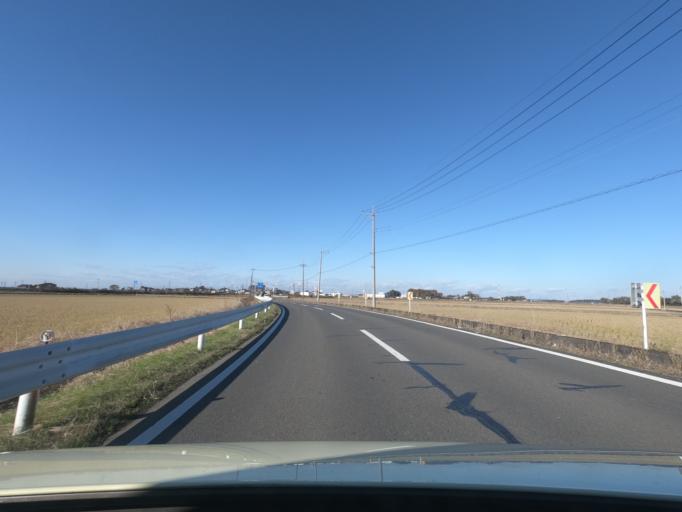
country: JP
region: Ibaraki
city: Ishige
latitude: 36.1566
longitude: 139.9972
